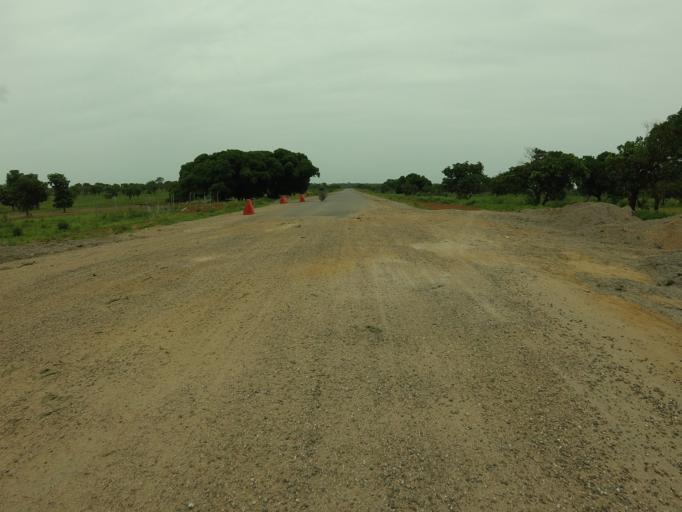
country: GH
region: Northern
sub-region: Yendi
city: Yendi
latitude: 9.2647
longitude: 0.0181
